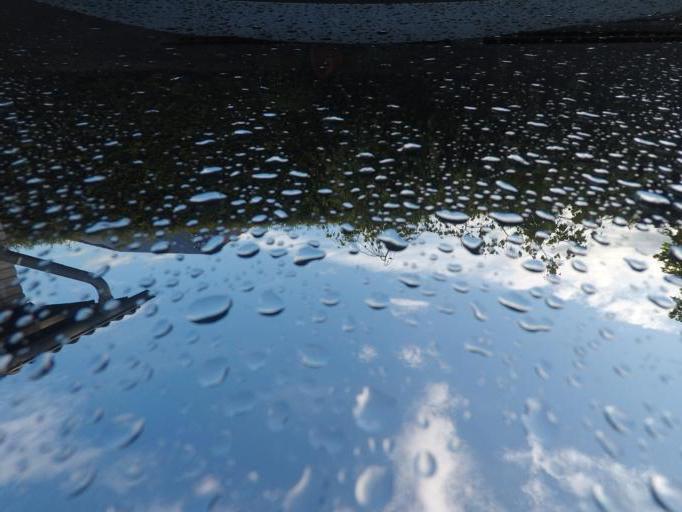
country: DE
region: Saxony-Anhalt
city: Kusey
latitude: 52.5877
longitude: 11.0953
